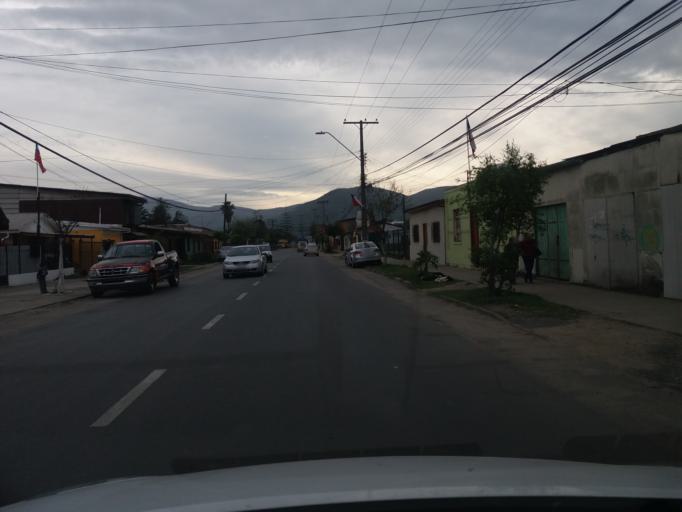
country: CL
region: Valparaiso
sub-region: Provincia de Quillota
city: Hacienda La Calera
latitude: -32.7781
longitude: -71.1896
